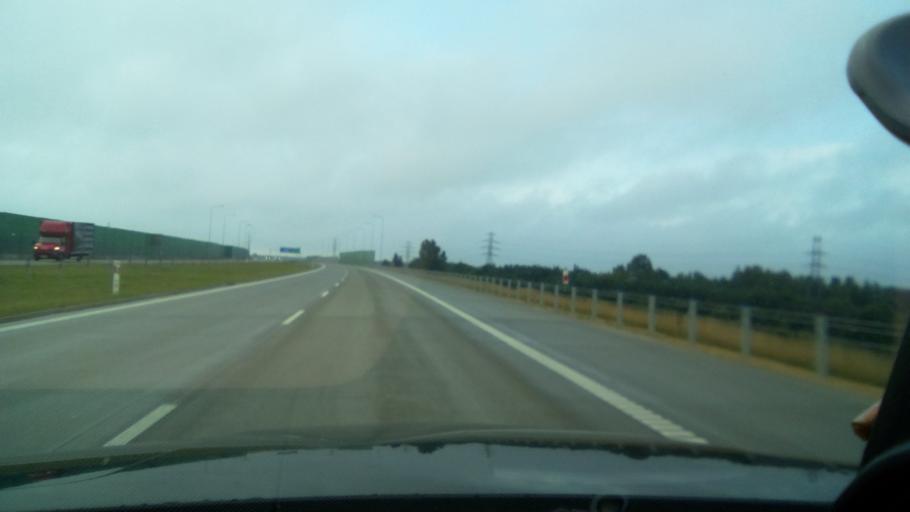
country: PL
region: Silesian Voivodeship
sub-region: Powiat czestochowski
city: Blachownia
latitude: 50.7879
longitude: 19.0016
